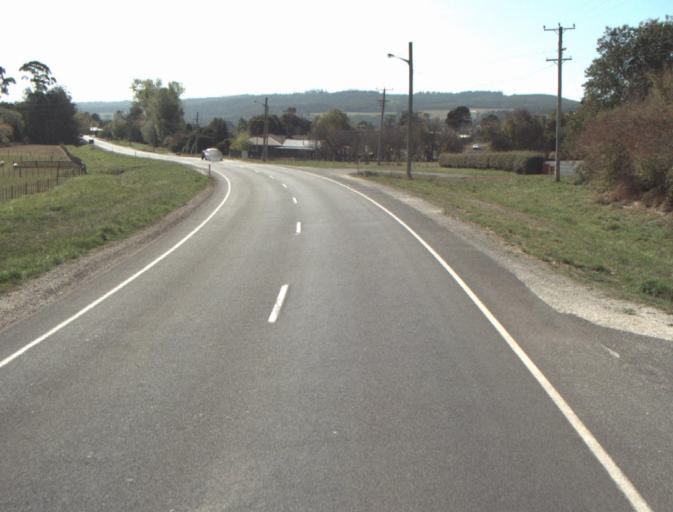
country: AU
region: Tasmania
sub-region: Launceston
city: Mayfield
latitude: -41.2594
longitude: 147.2181
